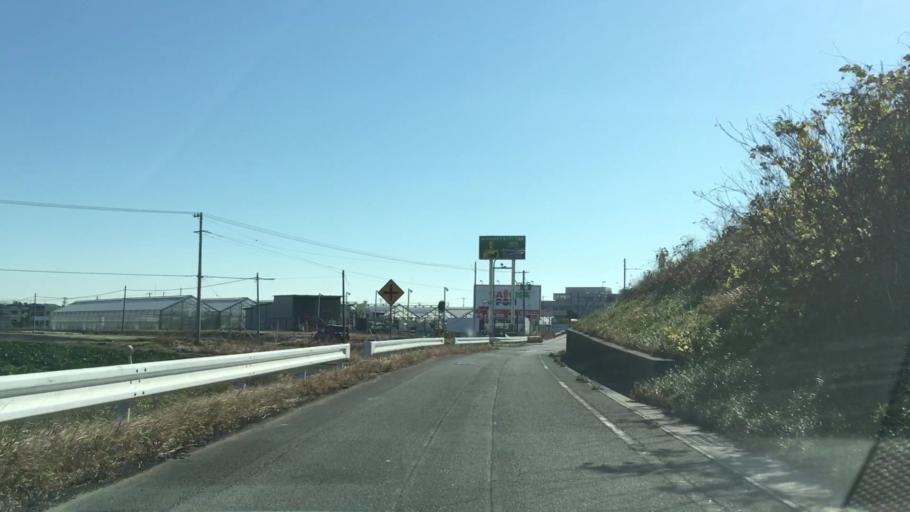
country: JP
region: Aichi
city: Toyohashi
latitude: 34.7296
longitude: 137.3542
